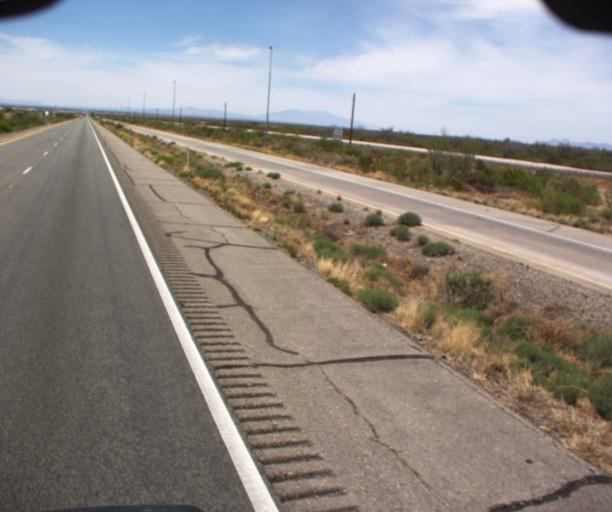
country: US
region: New Mexico
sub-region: Hidalgo County
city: Lordsburg
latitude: 32.2542
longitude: -109.1637
